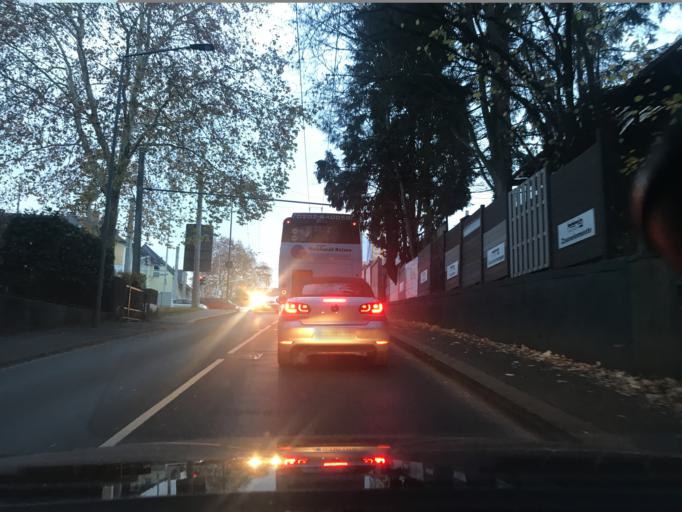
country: DE
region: North Rhine-Westphalia
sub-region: Regierungsbezirk Dusseldorf
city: Solingen
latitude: 51.1747
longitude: 7.0742
